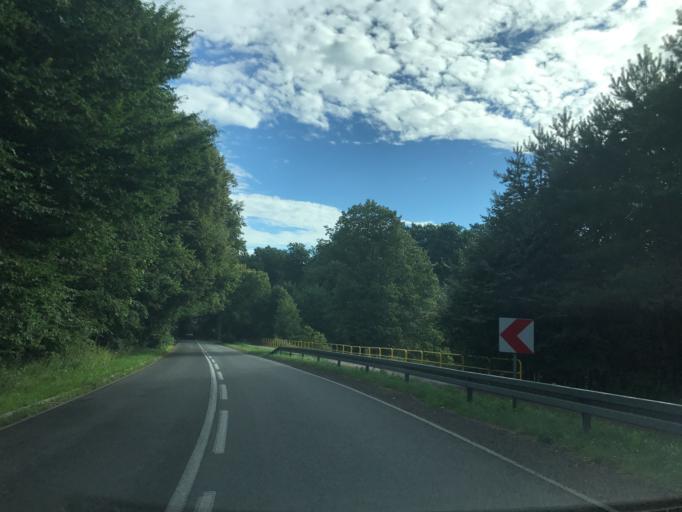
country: PL
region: West Pomeranian Voivodeship
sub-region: Powiat koszalinski
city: Sianow
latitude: 54.2138
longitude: 16.2732
